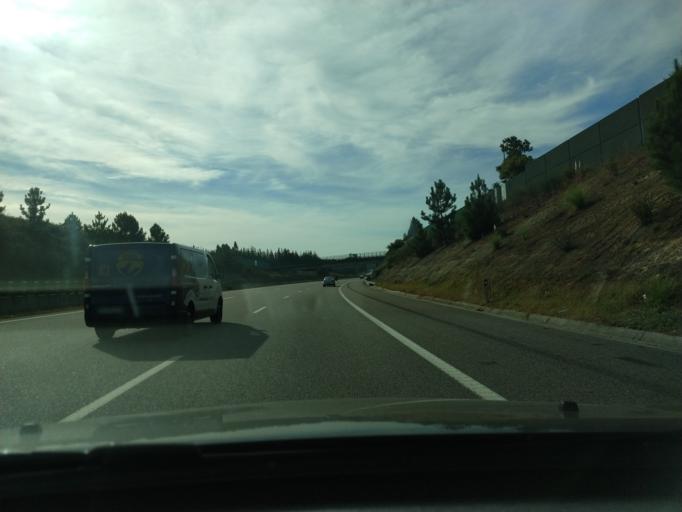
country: PT
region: Aveiro
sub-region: Ovar
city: Sao Joao
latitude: 40.8807
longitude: -8.5611
